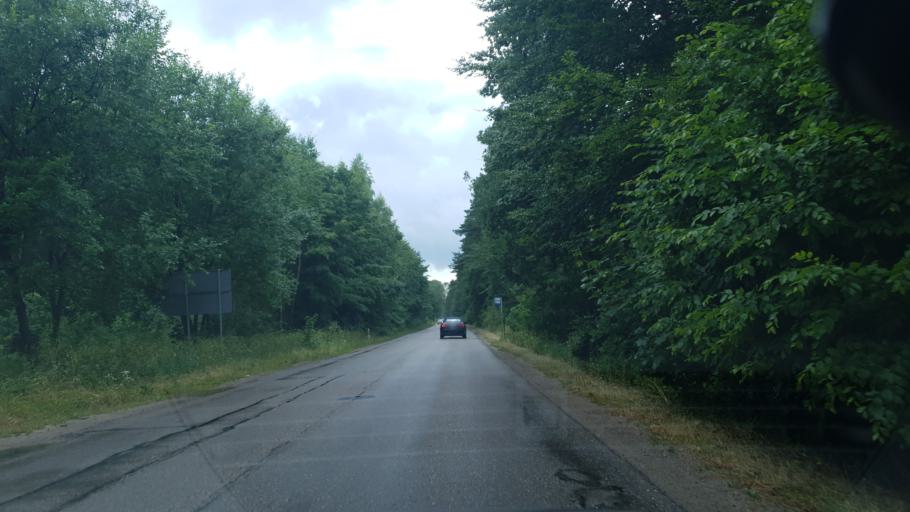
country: PL
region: Pomeranian Voivodeship
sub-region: Powiat kartuski
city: Chmielno
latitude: 54.2601
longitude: 18.0399
